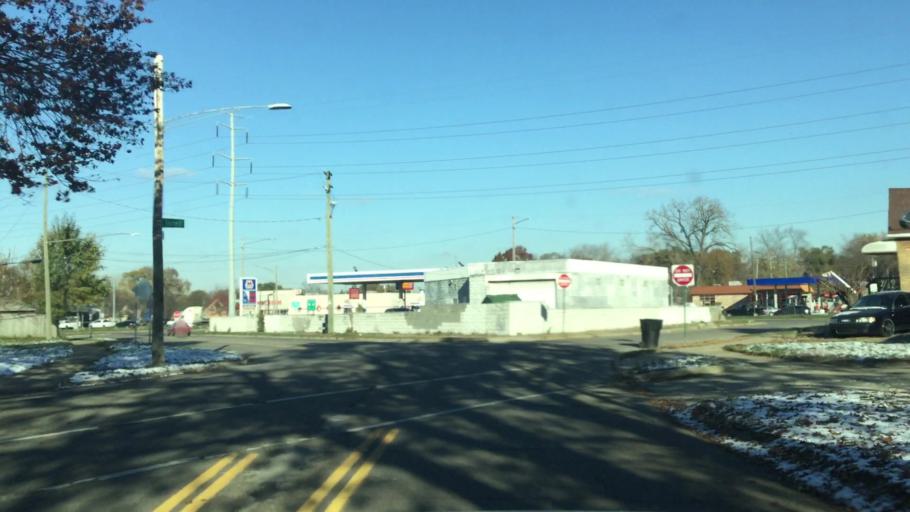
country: US
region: Michigan
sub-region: Macomb County
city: Warren
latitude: 42.4473
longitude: -83.0224
